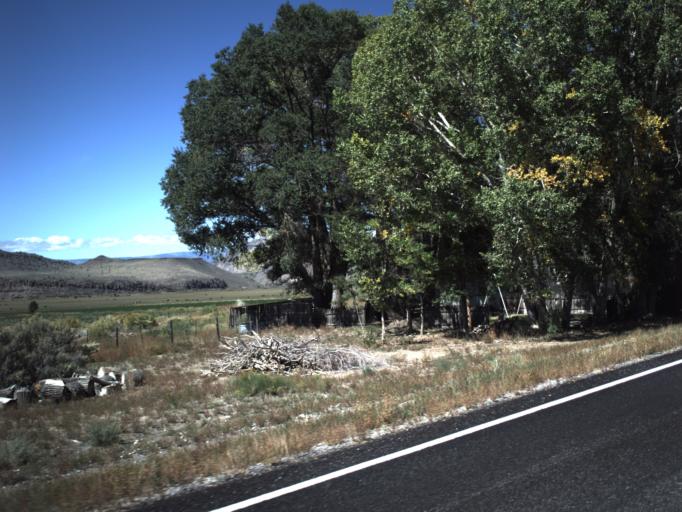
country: US
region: Utah
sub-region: Piute County
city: Junction
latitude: 38.1486
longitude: -112.0003
